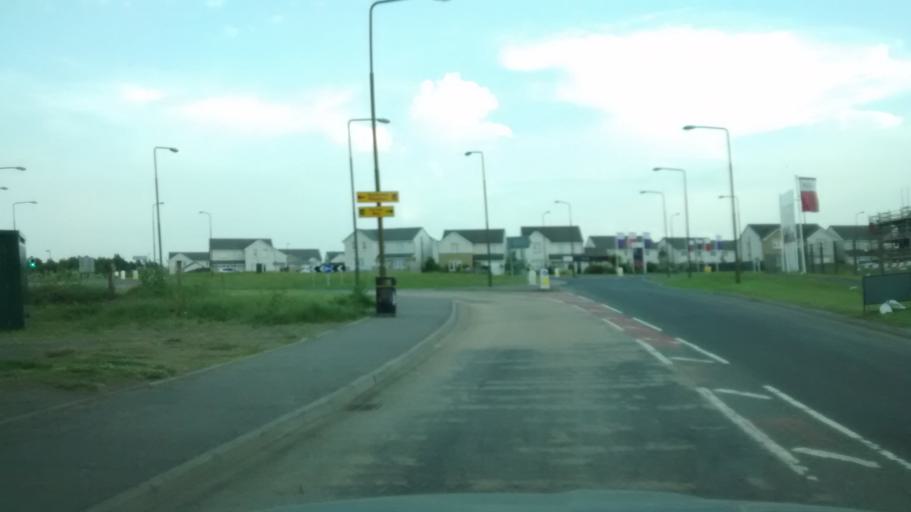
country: GB
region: Scotland
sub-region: West Lothian
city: Armadale
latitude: 55.8873
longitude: -3.6984
